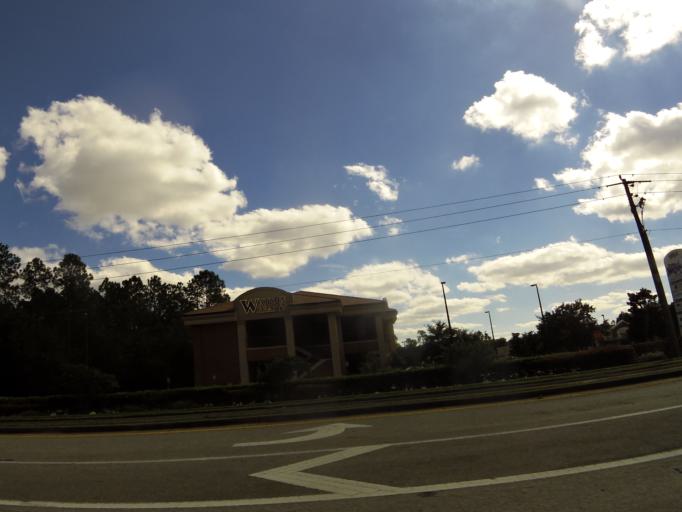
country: US
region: Florida
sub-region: Saint Johns County
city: Fruit Cove
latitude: 30.0575
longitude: -81.5395
